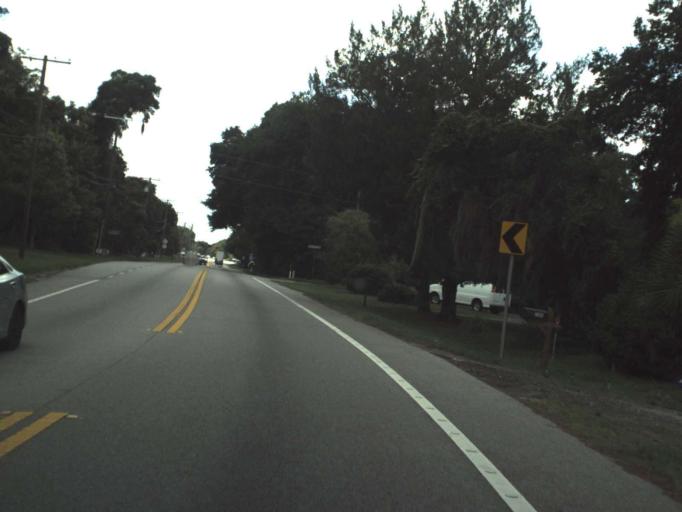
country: US
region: Florida
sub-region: Volusia County
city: DeLand
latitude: 29.0253
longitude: -81.2550
